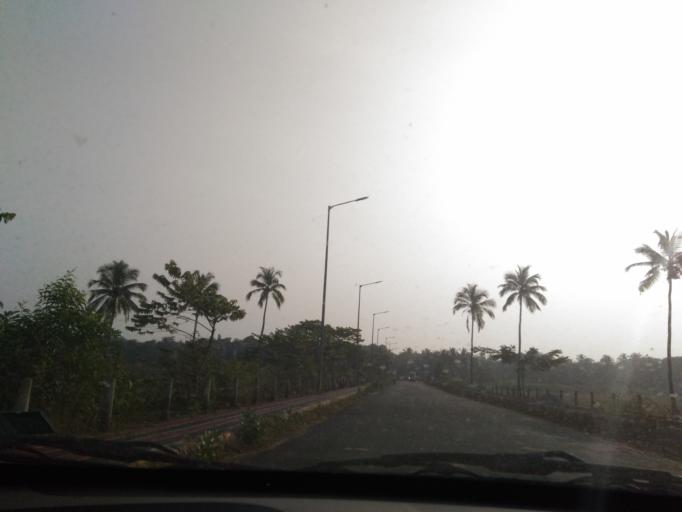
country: IN
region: Goa
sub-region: South Goa
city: Cuncolim
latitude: 15.1754
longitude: 73.9713
